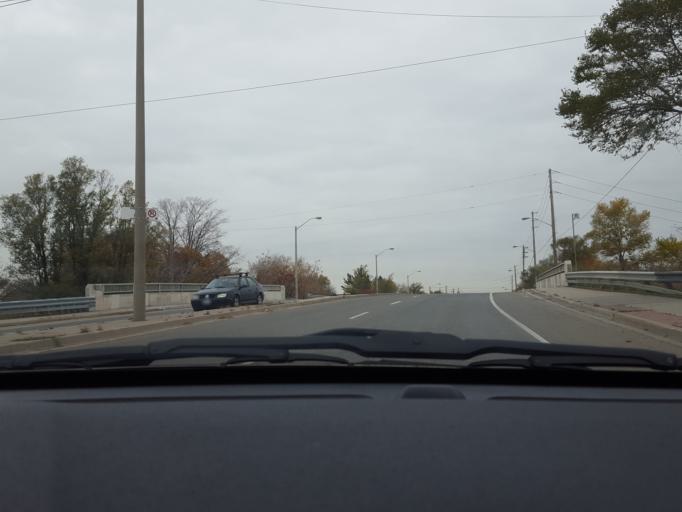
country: CA
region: Ontario
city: Etobicoke
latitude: 43.5935
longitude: -79.5414
